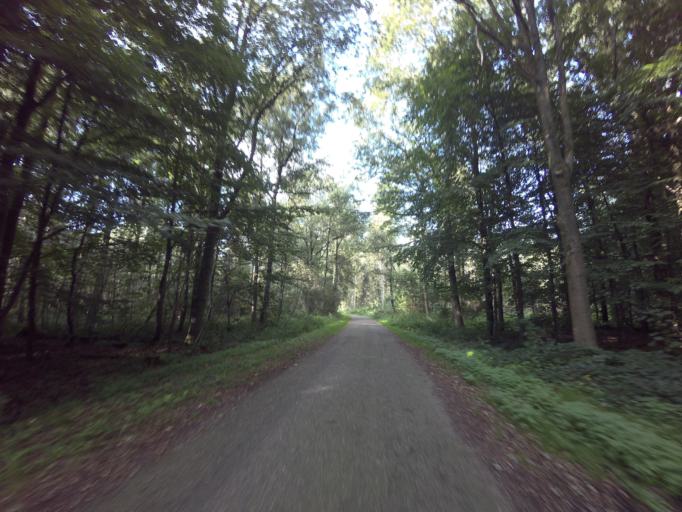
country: NL
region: Flevoland
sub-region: Gemeente Noordoostpolder
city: Ens
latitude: 52.6483
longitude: 5.7732
